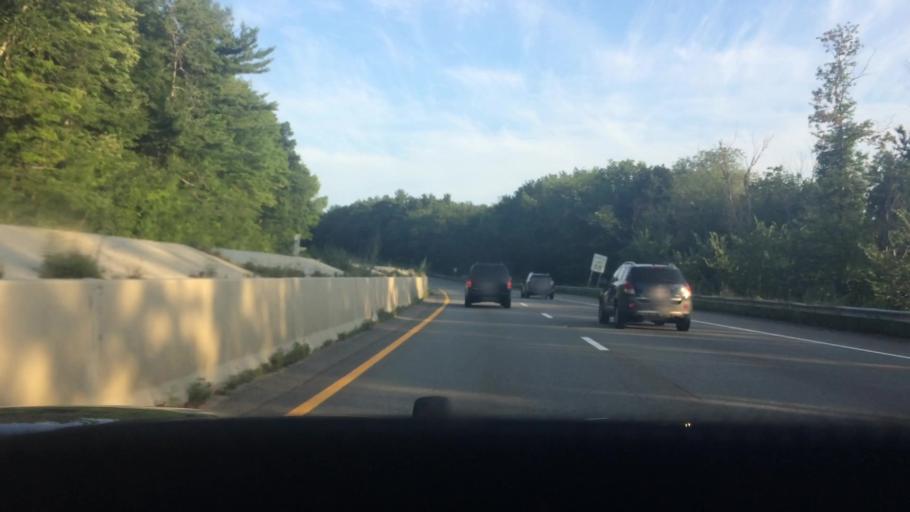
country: US
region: Massachusetts
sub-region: Worcester County
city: Leominster
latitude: 42.5502
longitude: -71.7656
